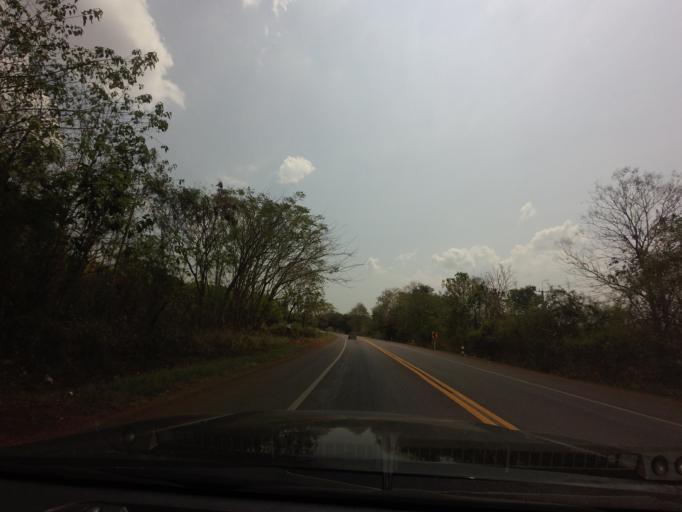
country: TH
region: Kanchanaburi
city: Sai Yok
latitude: 14.1388
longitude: 99.1492
